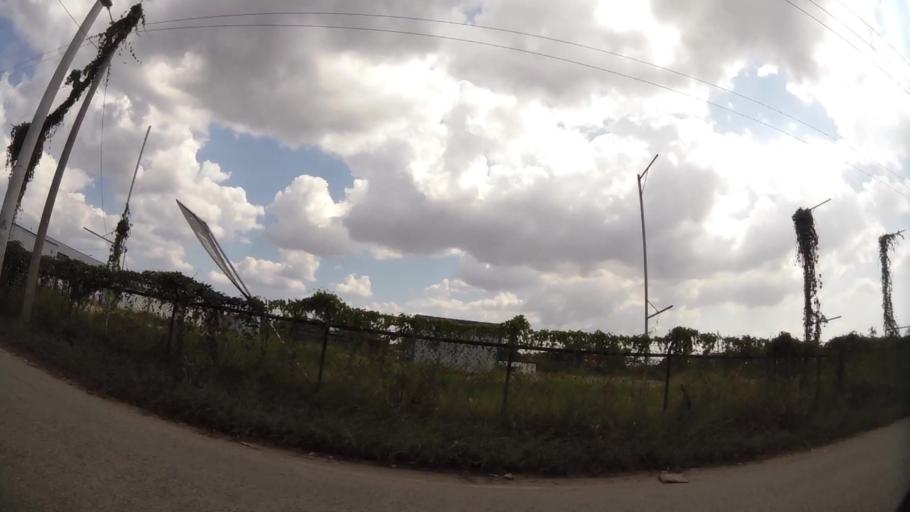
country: CO
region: Bolivar
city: Cartagena
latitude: 10.3752
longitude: -75.4622
